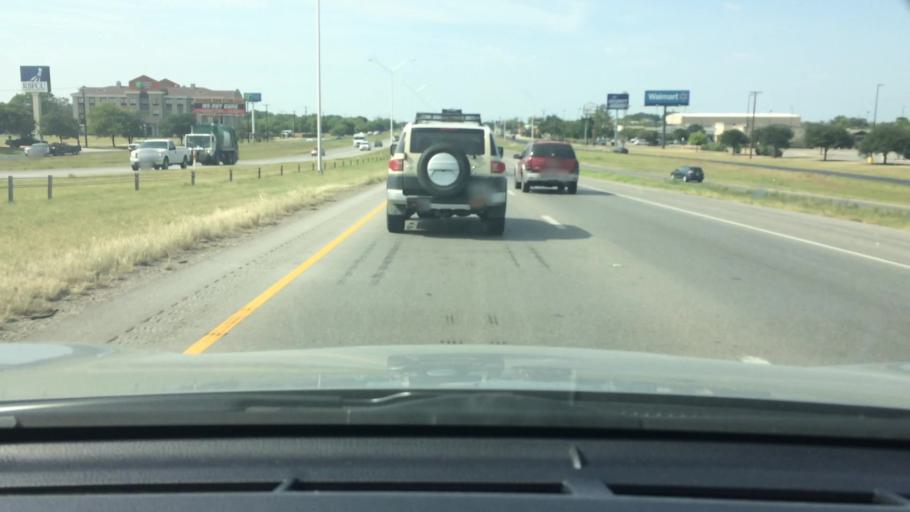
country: US
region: Texas
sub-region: Bexar County
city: China Grove
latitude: 29.3993
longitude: -98.3892
